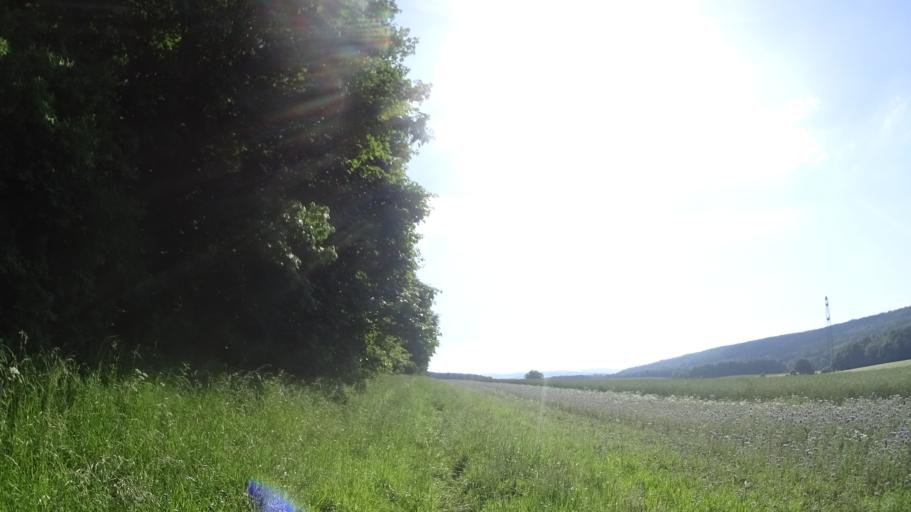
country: DE
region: Lower Saxony
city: Elbe
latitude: 52.1072
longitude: 10.2806
